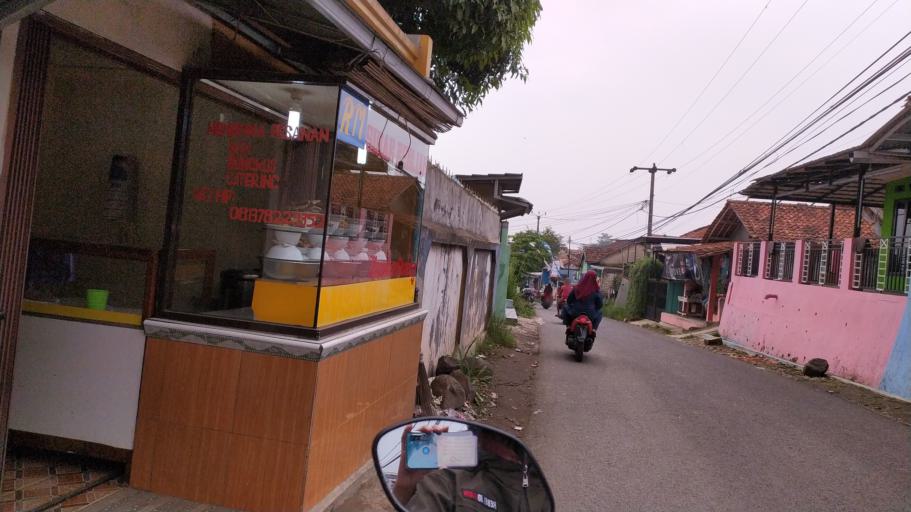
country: ID
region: West Java
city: Ciampea
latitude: -6.5871
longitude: 106.7056
